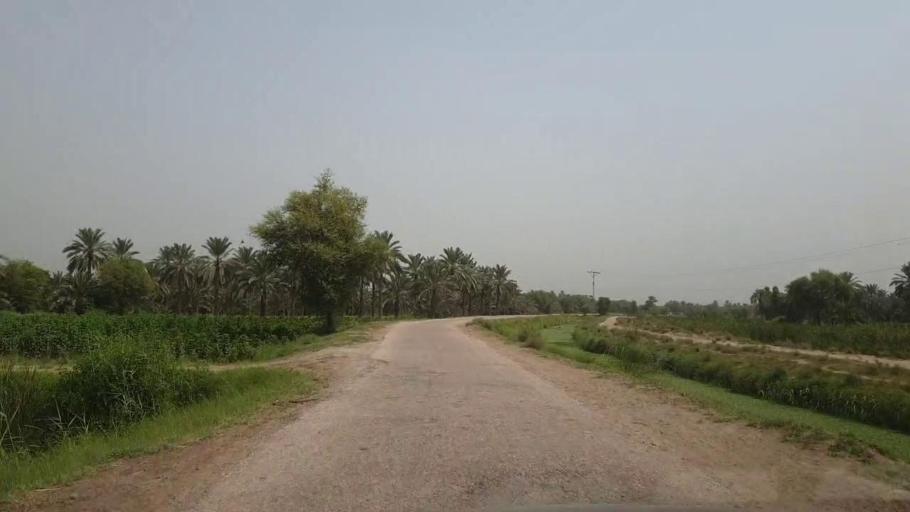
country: PK
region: Sindh
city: Gambat
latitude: 27.4195
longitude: 68.5537
